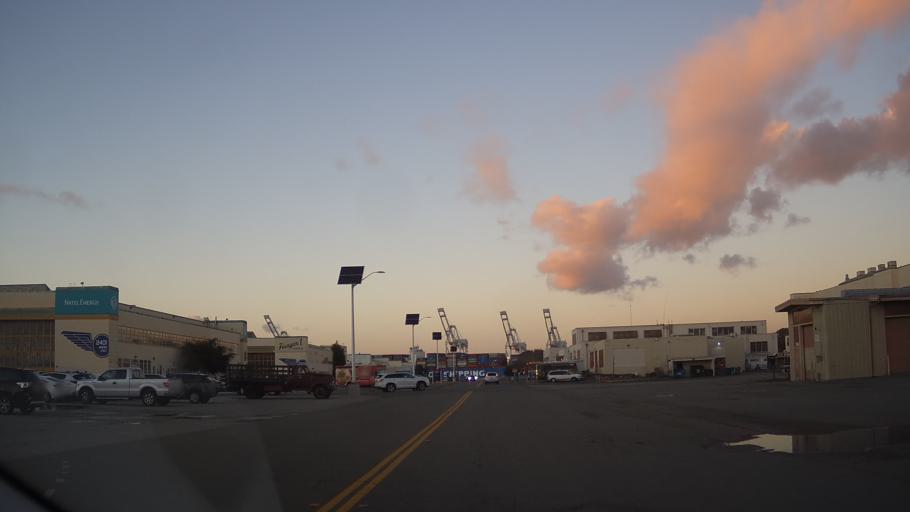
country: US
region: California
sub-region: Alameda County
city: Oakland
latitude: 37.7843
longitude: -122.3085
